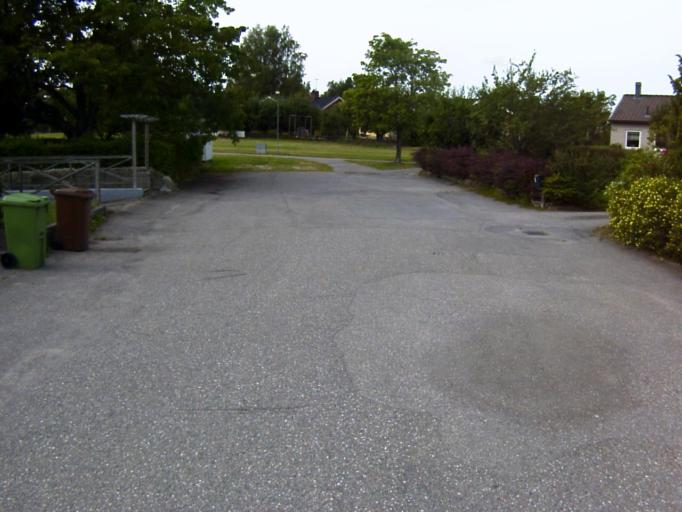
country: SE
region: Soedermanland
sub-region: Eskilstuna Kommun
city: Arla
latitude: 59.3877
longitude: 16.6835
